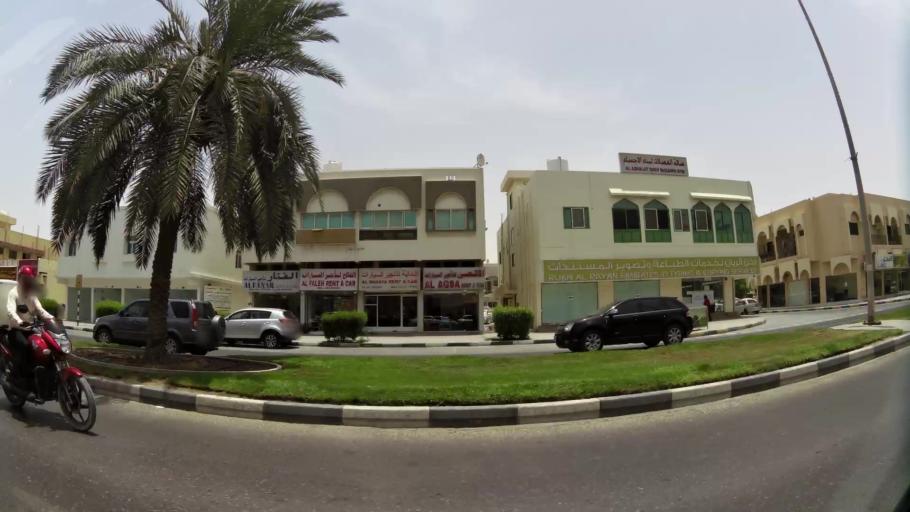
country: AE
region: Ash Shariqah
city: Sharjah
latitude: 25.3512
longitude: 55.4005
